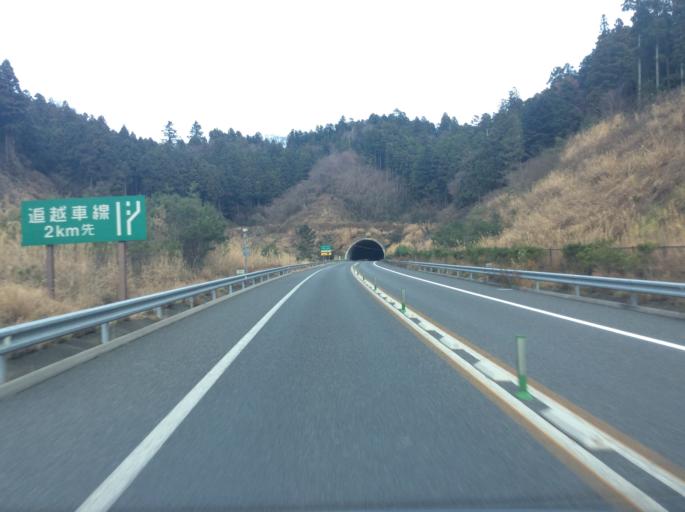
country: JP
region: Fukushima
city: Iwaki
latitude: 37.1721
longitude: 140.9702
